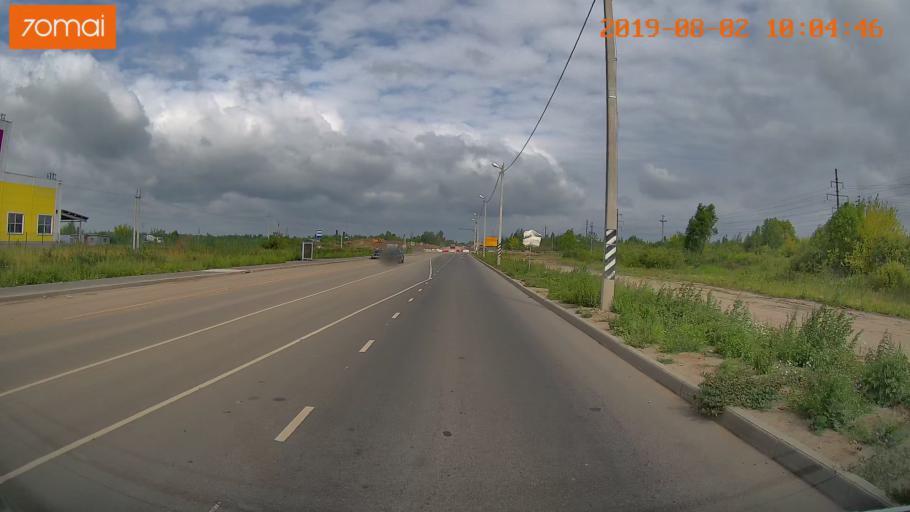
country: RU
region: Ivanovo
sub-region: Gorod Ivanovo
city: Ivanovo
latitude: 56.9752
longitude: 40.9228
